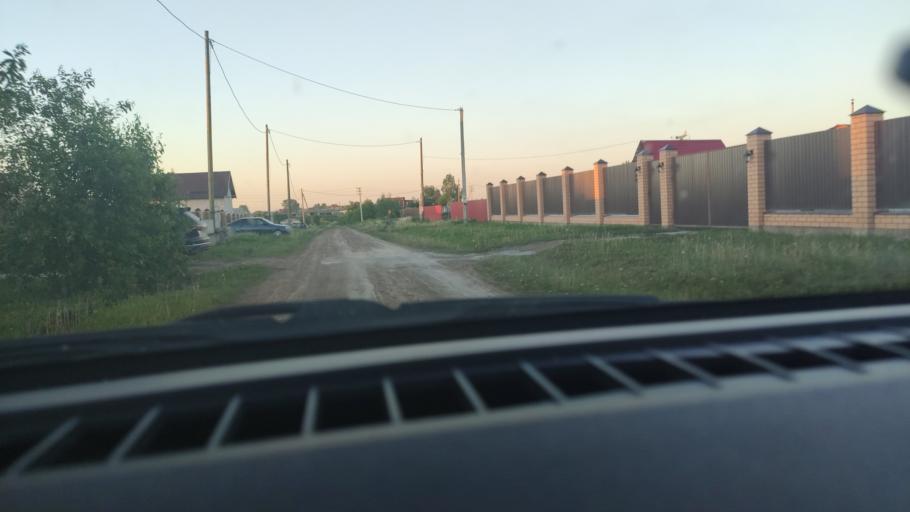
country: RU
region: Perm
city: Kultayevo
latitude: 57.9038
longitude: 55.9763
